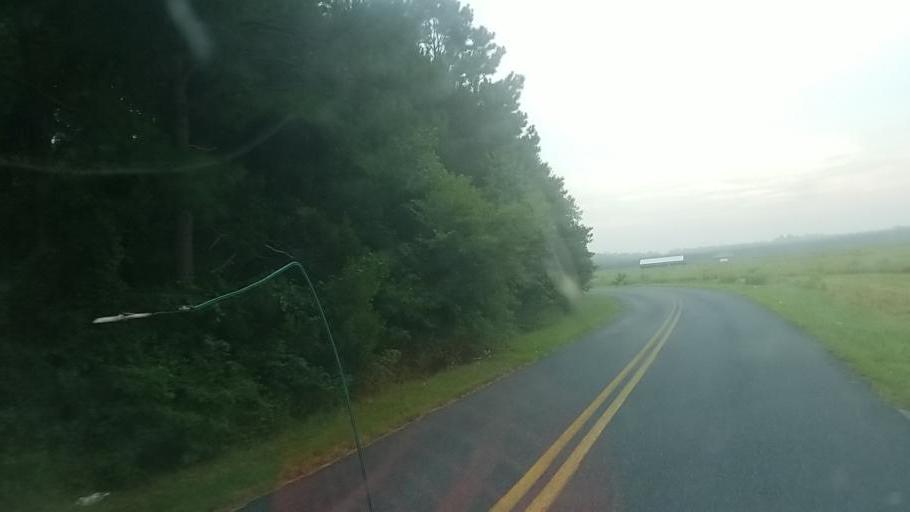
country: US
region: Maryland
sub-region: Wicomico County
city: Delmar
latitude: 38.4142
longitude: -75.5004
